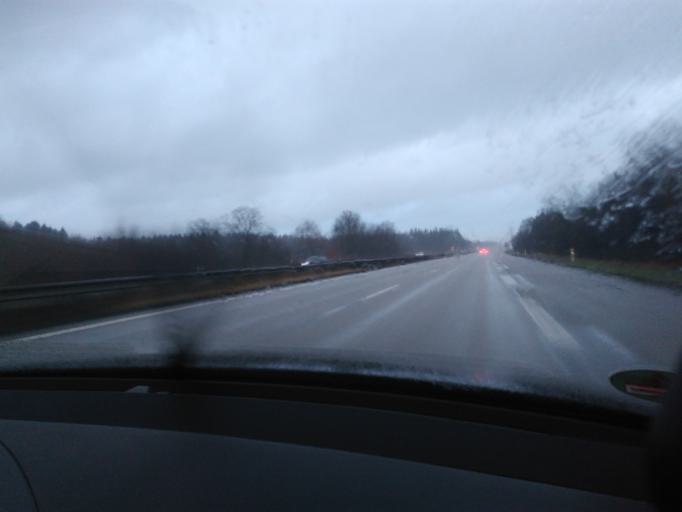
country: DE
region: Schleswig-Holstein
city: Bimohlen
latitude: 53.9198
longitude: 9.9387
